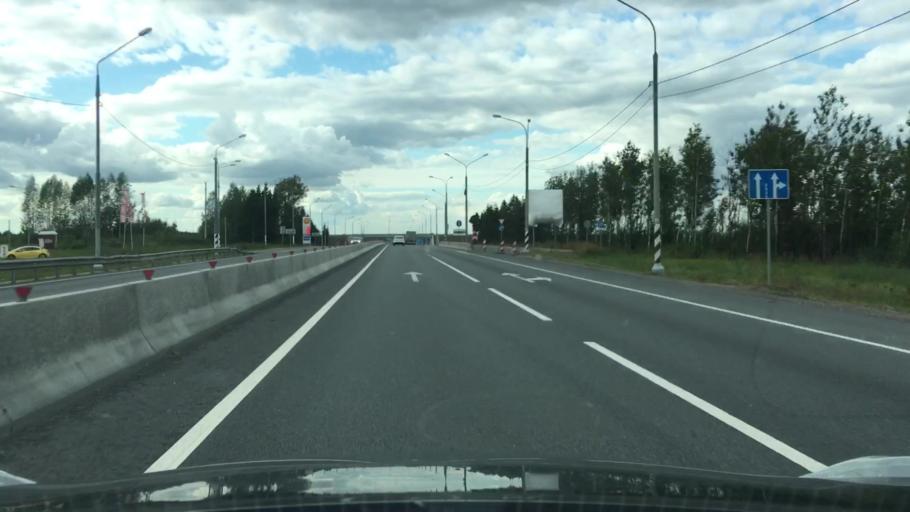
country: RU
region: Tverskaya
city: Tver
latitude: 56.7856
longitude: 35.9300
